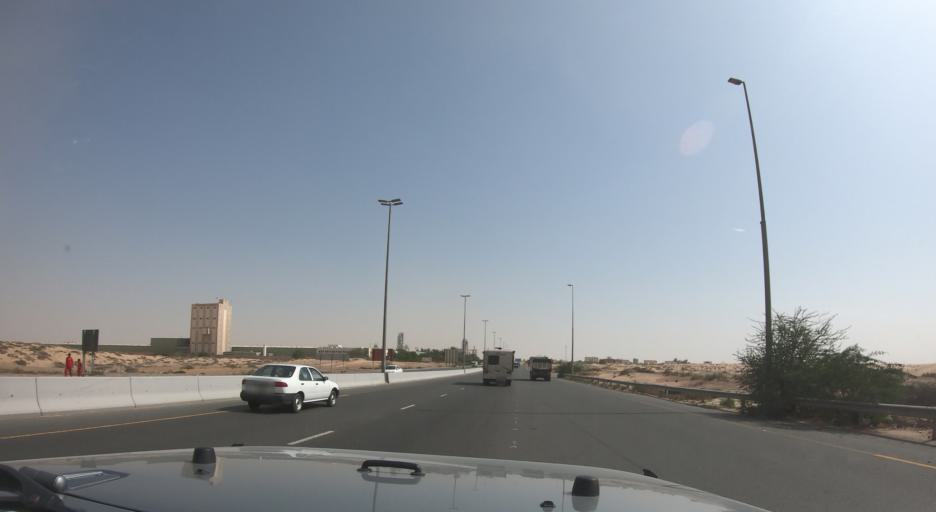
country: AE
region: Ash Shariqah
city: Sharjah
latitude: 25.2996
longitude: 55.6008
